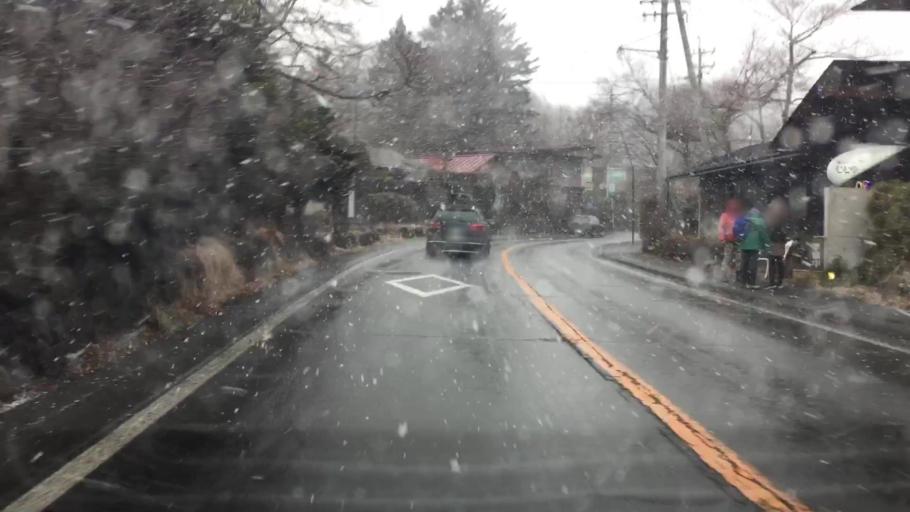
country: JP
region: Nagano
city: Komoro
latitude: 36.3540
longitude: 138.5899
